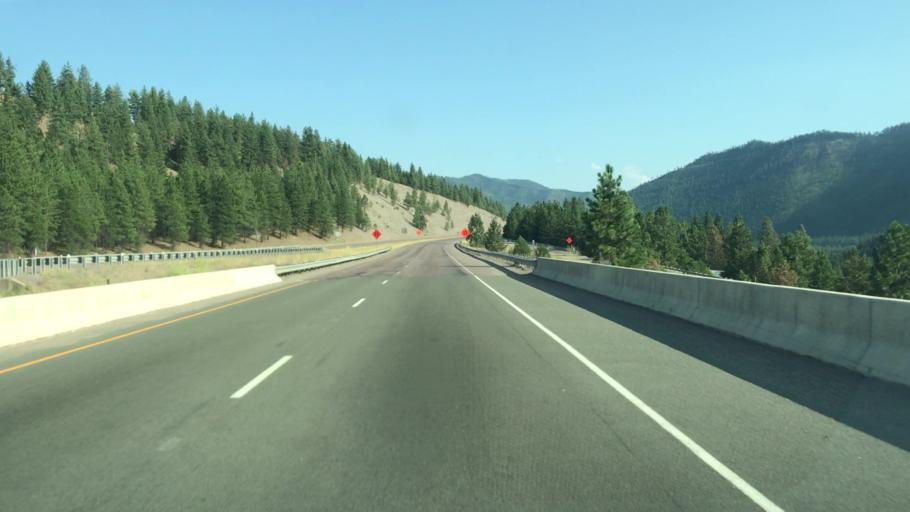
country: US
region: Montana
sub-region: Mineral County
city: Superior
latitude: 47.0260
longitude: -114.7395
